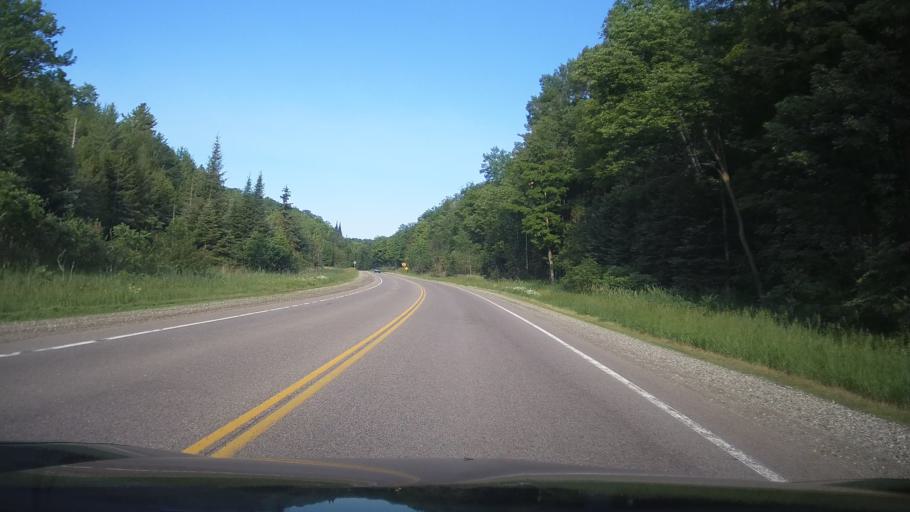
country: CA
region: Ontario
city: Perth
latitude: 44.7663
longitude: -76.7569
